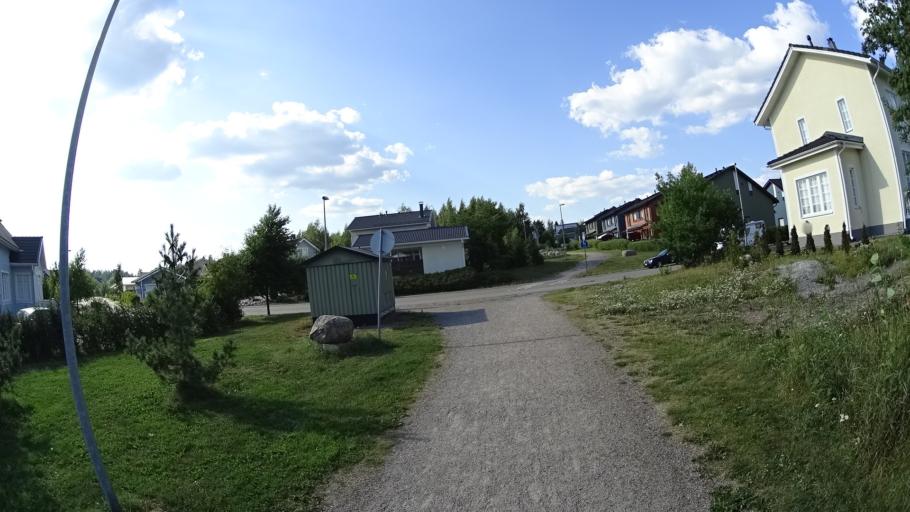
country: FI
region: Uusimaa
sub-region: Porvoo
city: Porvoo
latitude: 60.4127
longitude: 25.6603
